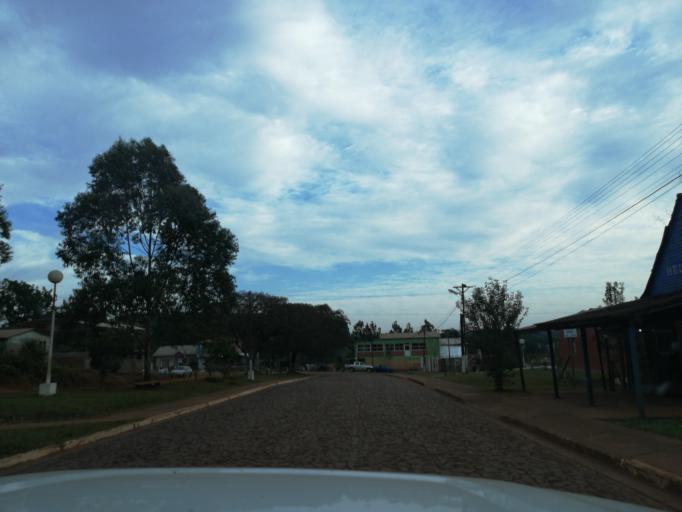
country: AR
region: Misiones
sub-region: Departamento de San Pedro
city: San Pedro
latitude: -26.6242
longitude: -54.0971
